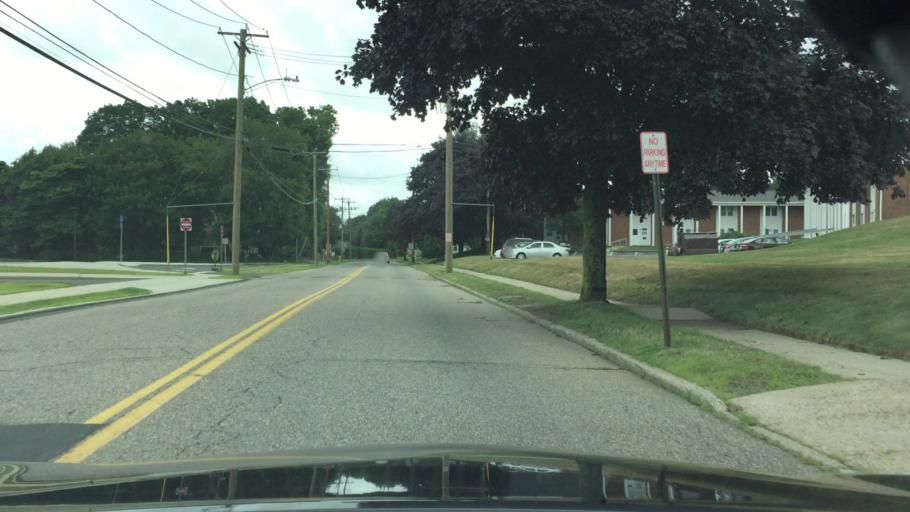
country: US
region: Connecticut
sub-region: New Haven County
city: City of Milford (balance)
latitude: 41.2111
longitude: -73.0744
